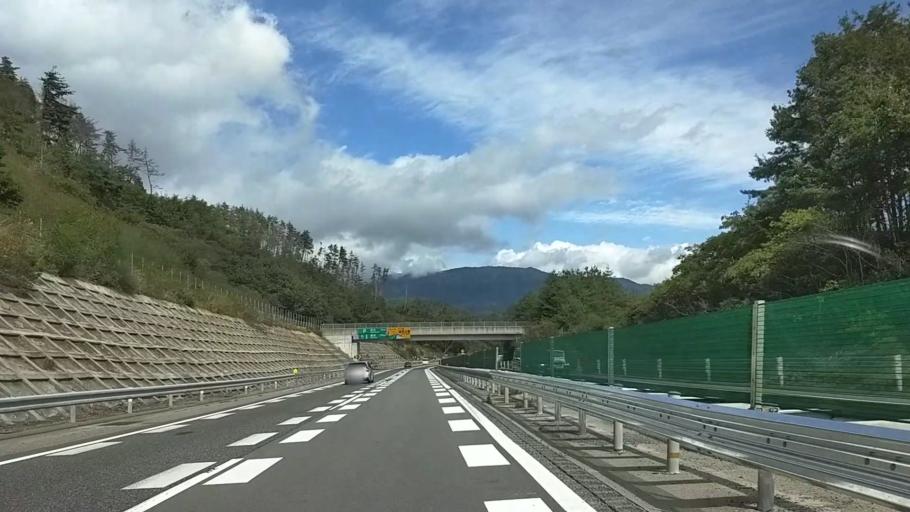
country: JP
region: Nagano
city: Hotaka
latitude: 36.4102
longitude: 138.0013
